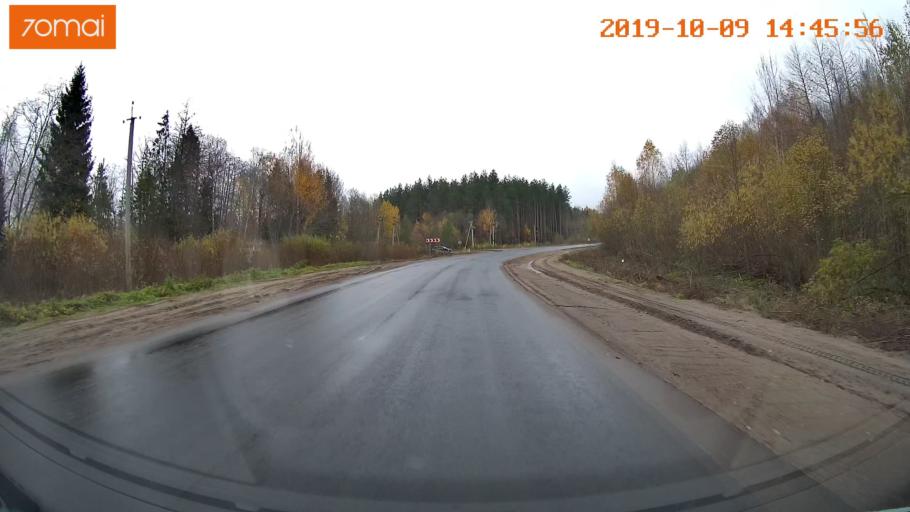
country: RU
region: Kostroma
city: Buy
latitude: 58.4376
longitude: 41.5769
